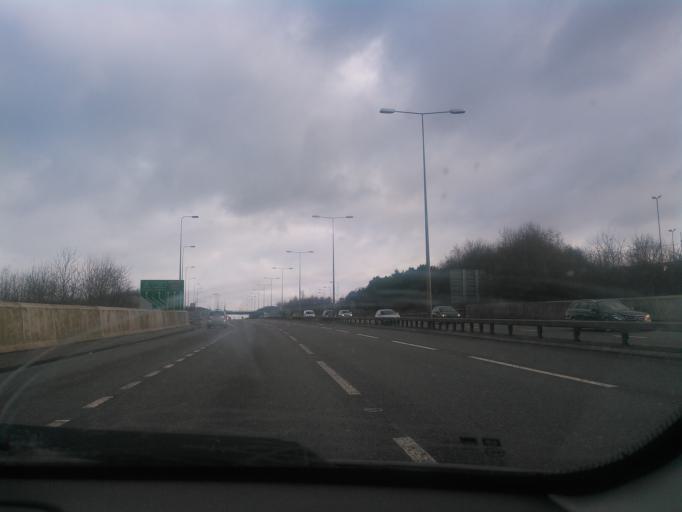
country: GB
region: England
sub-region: Stoke-on-Trent
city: Stoke-on-Trent
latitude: 52.9903
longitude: -2.1788
